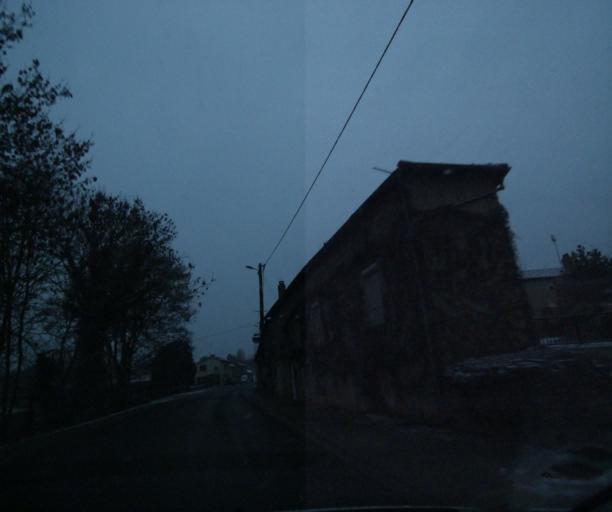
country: FR
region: Champagne-Ardenne
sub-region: Departement de la Haute-Marne
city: Wassy
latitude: 48.4378
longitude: 4.9597
